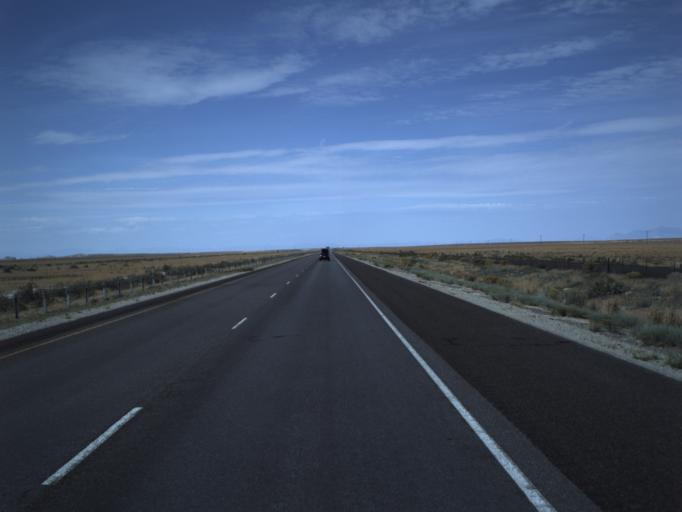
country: US
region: Utah
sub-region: Tooele County
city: Grantsville
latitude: 40.7268
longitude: -113.2101
